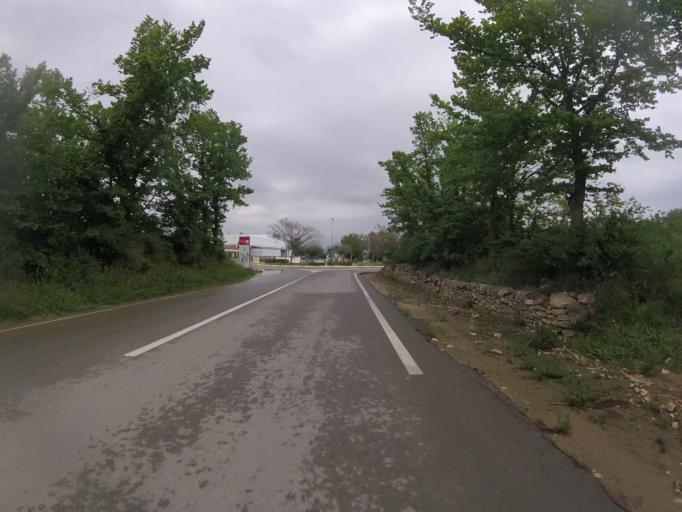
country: ES
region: Valencia
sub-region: Provincia de Castello
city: Alcala de Xivert
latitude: 40.3094
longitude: 0.2293
